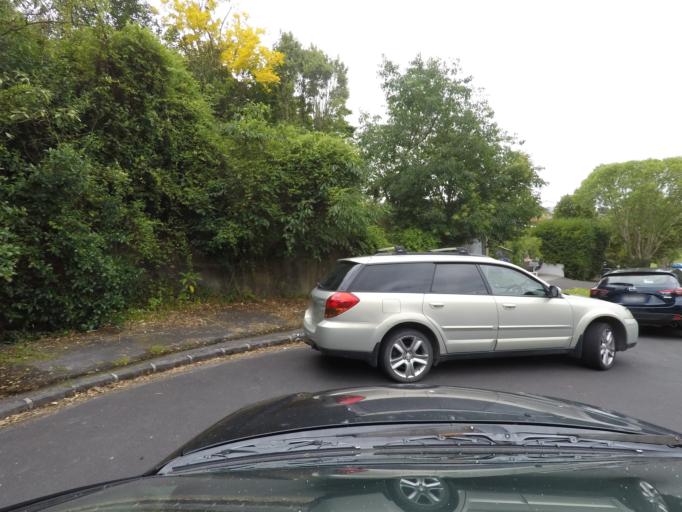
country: NZ
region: Auckland
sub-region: Auckland
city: Auckland
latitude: -36.8666
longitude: 174.7363
